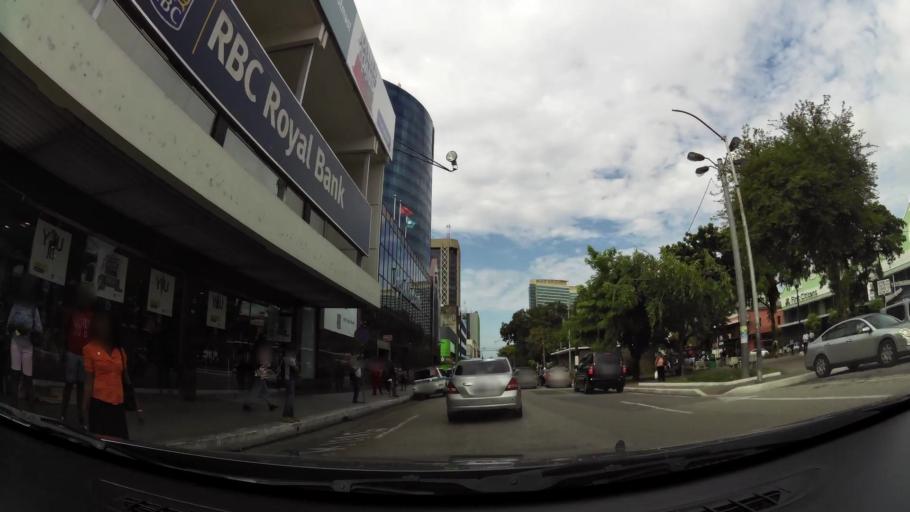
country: TT
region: San Juan/Laventille
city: Laventille
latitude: 10.6496
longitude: -61.5097
